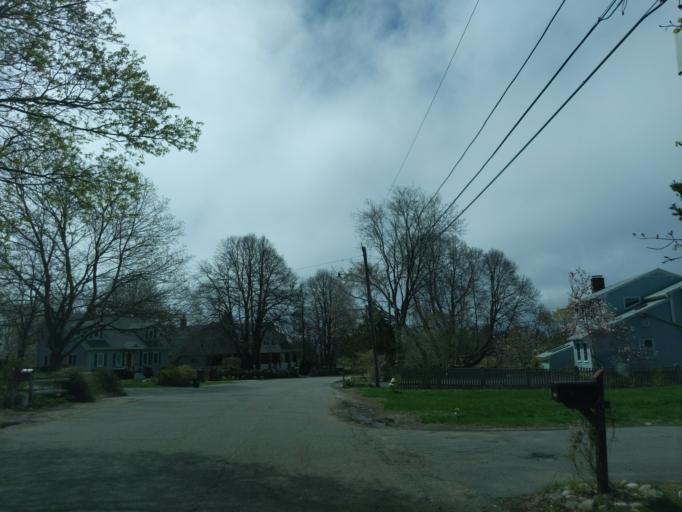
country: US
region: Massachusetts
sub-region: Essex County
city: Rockport
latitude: 42.6406
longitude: -70.6002
